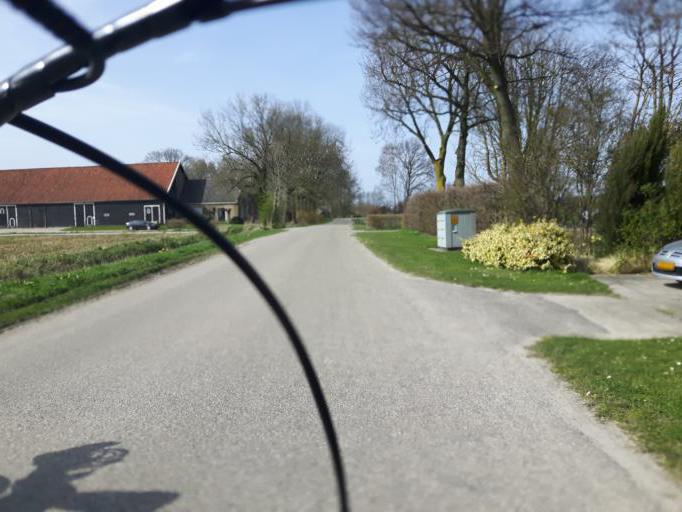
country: NL
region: Zeeland
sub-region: Gemeente Goes
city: Goes
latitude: 51.4836
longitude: 3.9157
